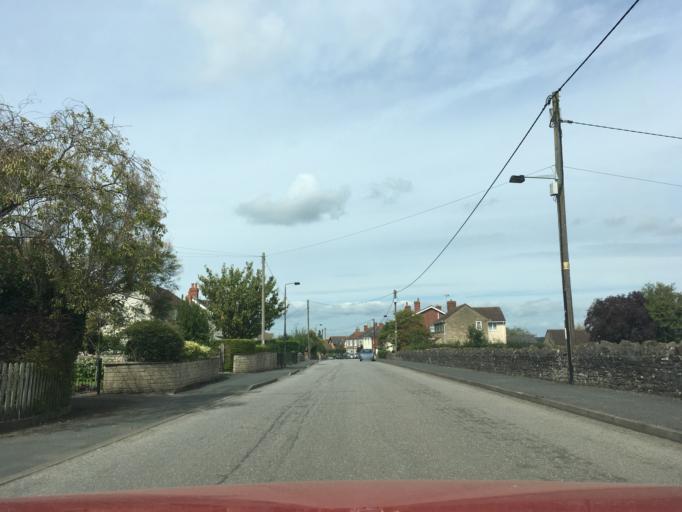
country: GB
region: England
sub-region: South Gloucestershire
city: Charfield
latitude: 51.6299
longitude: -2.3991
